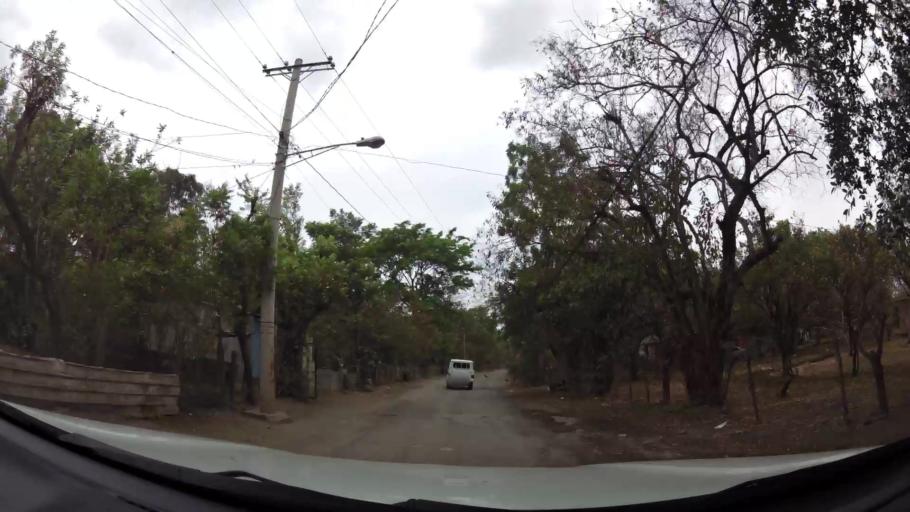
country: NI
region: Masaya
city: Ticuantepe
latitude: 12.0806
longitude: -86.1900
